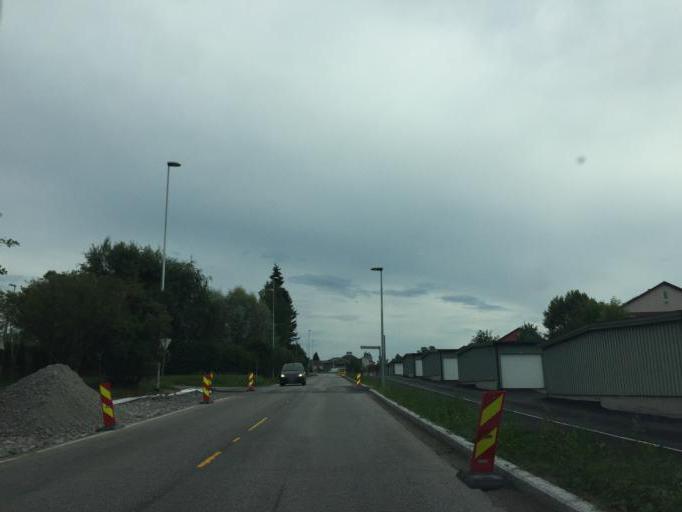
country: NO
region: Hedmark
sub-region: Kongsvinger
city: Kongsvinger
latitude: 60.2021
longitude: 11.9823
